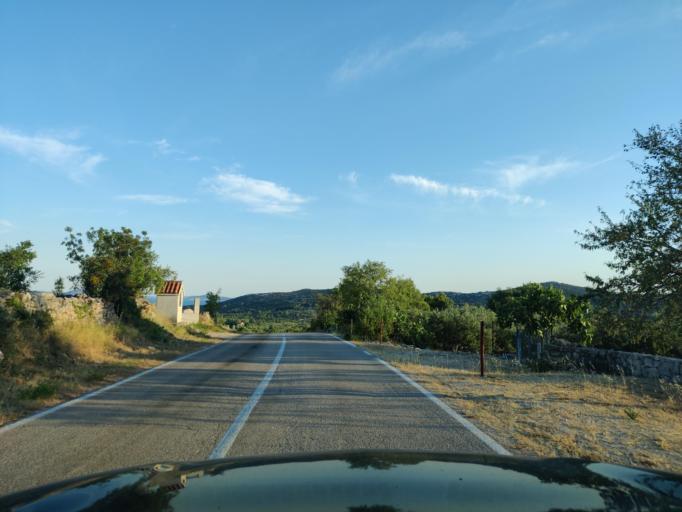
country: HR
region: Sibensko-Kniniska
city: Tribunj
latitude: 43.7872
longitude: 15.7267
